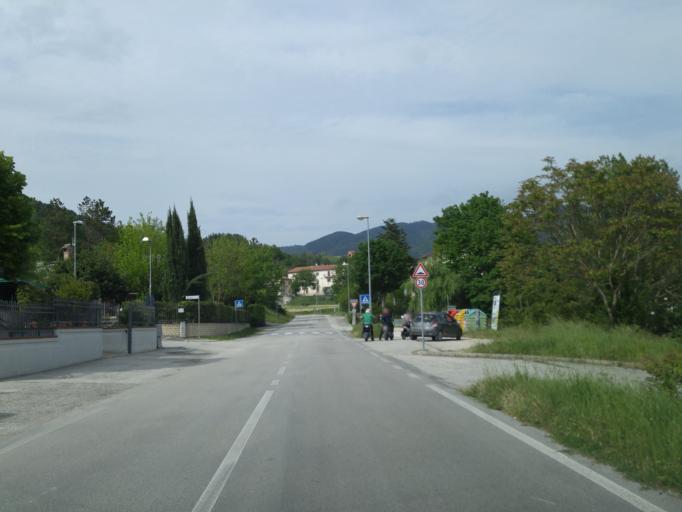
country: IT
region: The Marches
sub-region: Provincia di Pesaro e Urbino
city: Acqualagna
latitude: 43.6264
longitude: 12.6736
